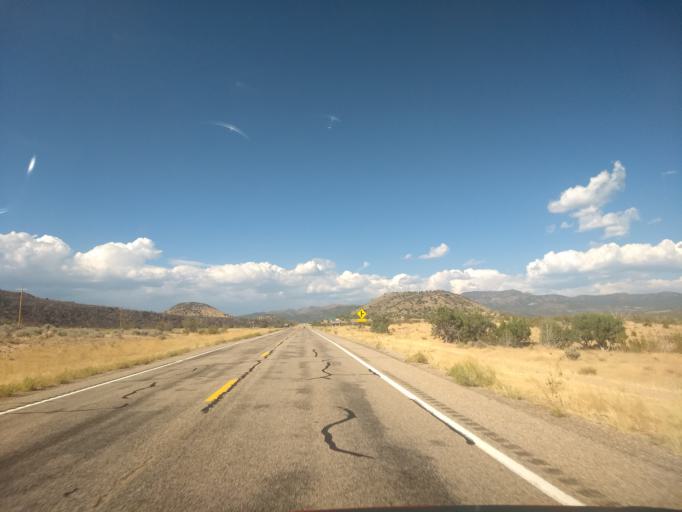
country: US
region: Utah
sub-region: Washington County
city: Enterprise
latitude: 37.3825
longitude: -113.6517
